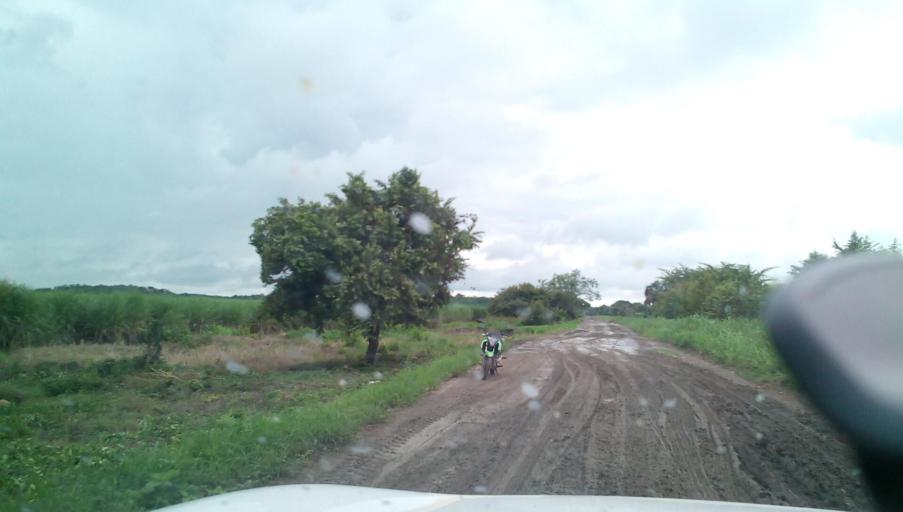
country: MX
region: Veracruz
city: Panuco
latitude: 21.8218
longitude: -98.1108
